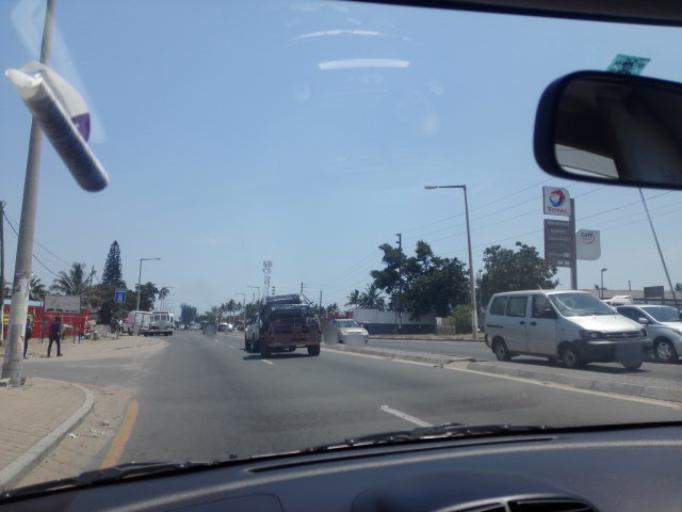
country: MZ
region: Maputo City
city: Maputo
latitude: -25.9043
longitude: 32.5655
